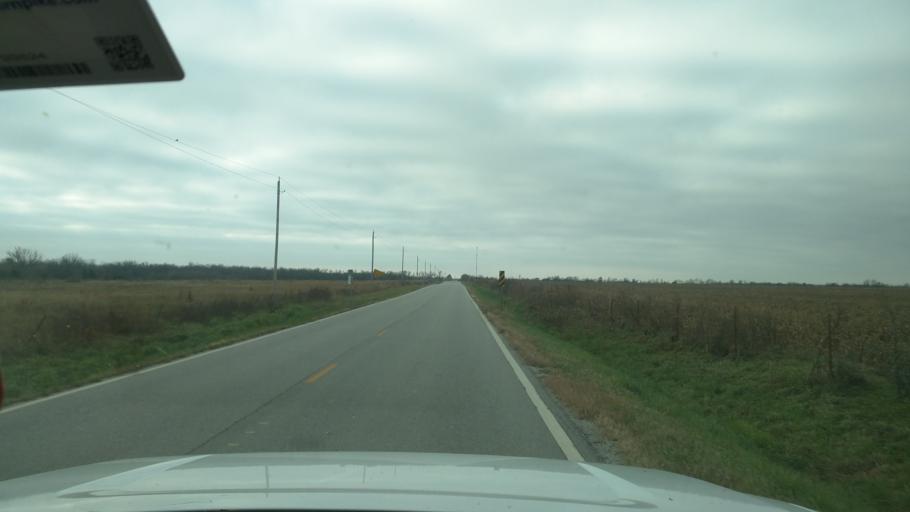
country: US
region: Kansas
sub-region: Elk County
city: Howard
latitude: 37.6496
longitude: -96.2346
